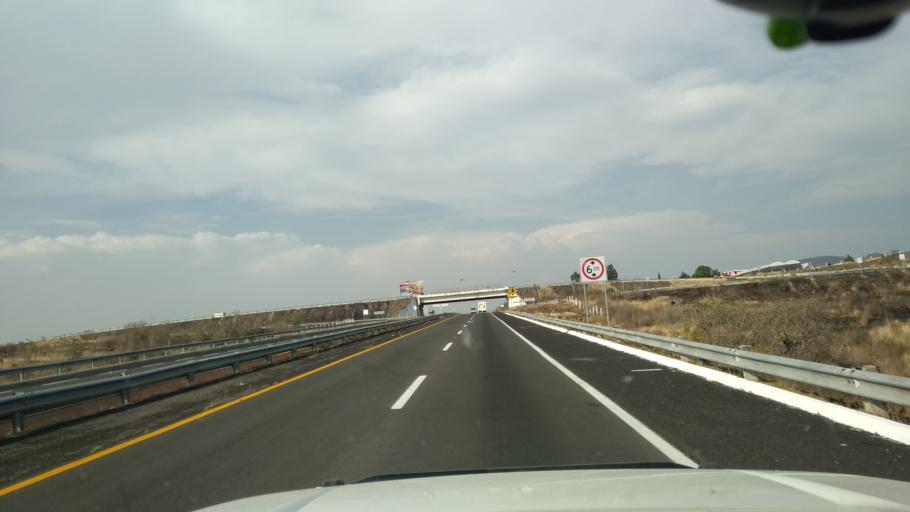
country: MX
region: Puebla
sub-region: Atlixco
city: San Agustin Huixaxtla
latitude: 18.9358
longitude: -98.3924
